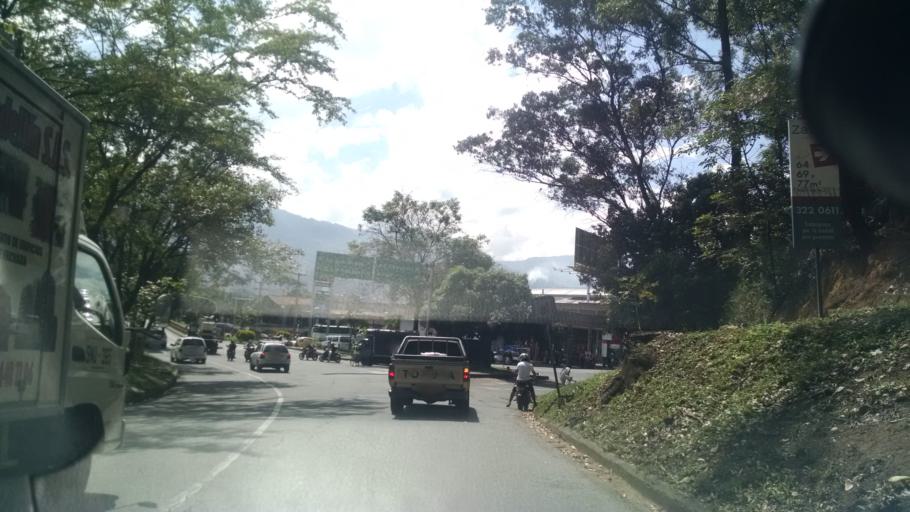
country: CO
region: Antioquia
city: Itagui
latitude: 6.2053
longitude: -75.5888
